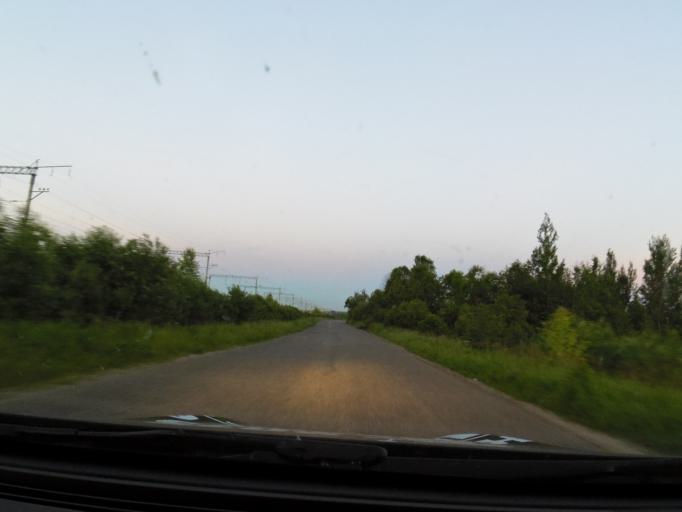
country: RU
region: Kostroma
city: Buy
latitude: 58.4850
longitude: 41.5068
